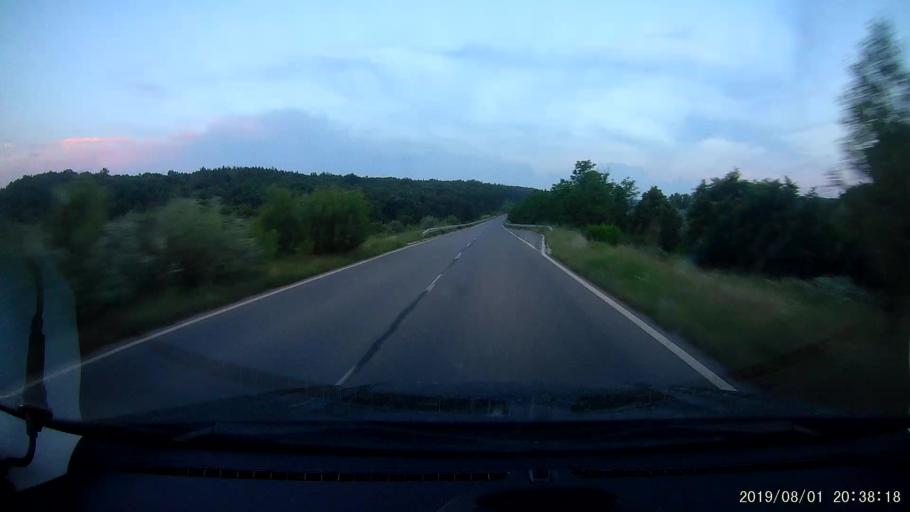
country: BG
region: Yambol
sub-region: Obshtina Elkhovo
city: Elkhovo
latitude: 42.0295
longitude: 26.6002
